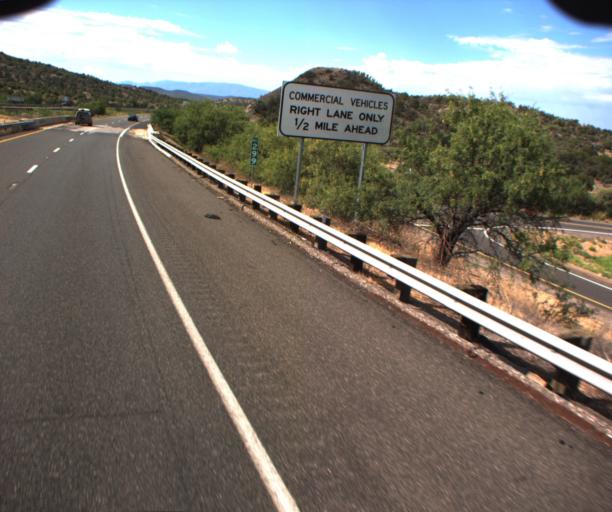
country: US
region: Arizona
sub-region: Yavapai County
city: Lake Montezuma
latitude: 34.6910
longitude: -111.7435
